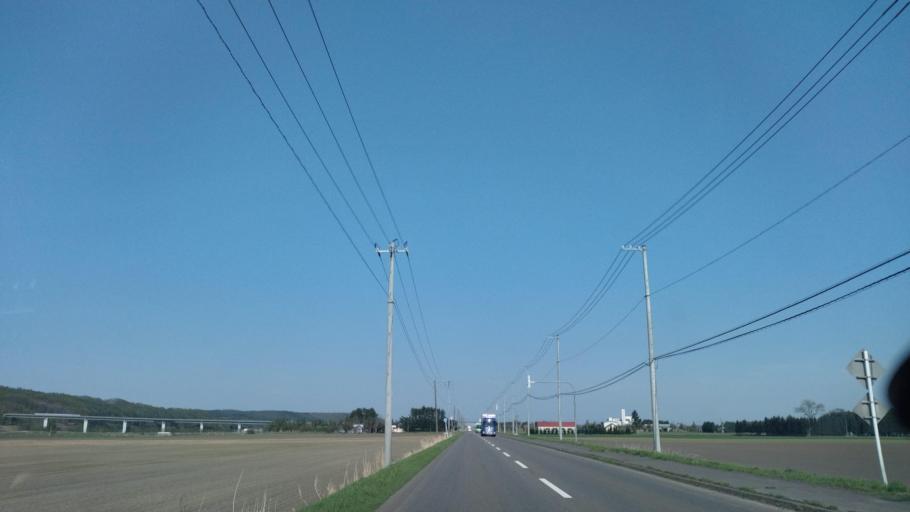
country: JP
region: Hokkaido
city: Obihiro
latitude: 42.9442
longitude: 143.0936
